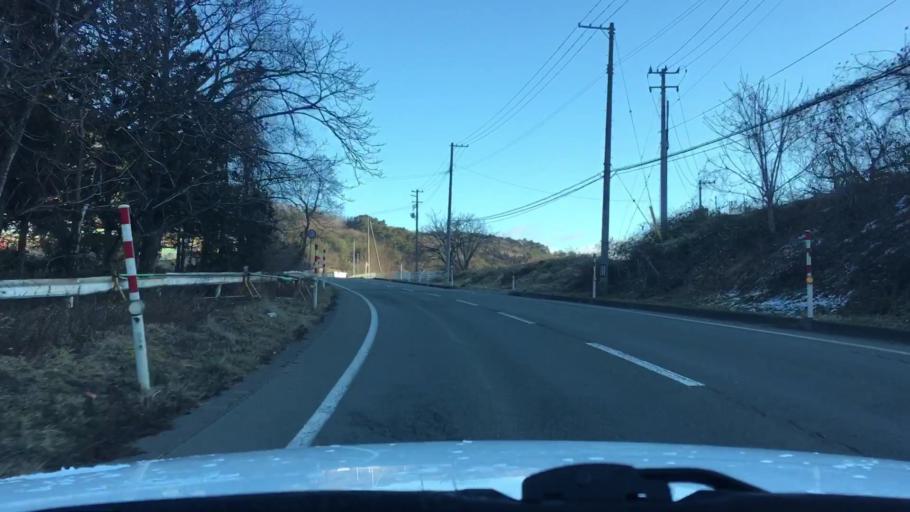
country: JP
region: Iwate
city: Morioka-shi
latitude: 39.6578
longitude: 141.1919
